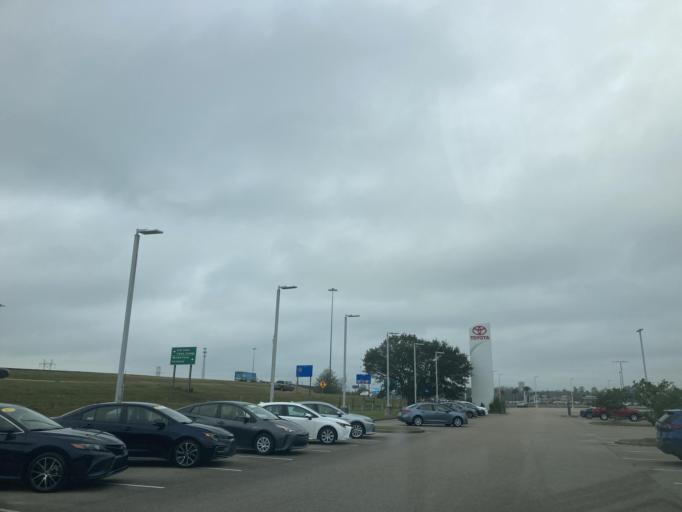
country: US
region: Mississippi
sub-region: Harrison County
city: West Gulfport
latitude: 30.4455
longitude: -89.0286
